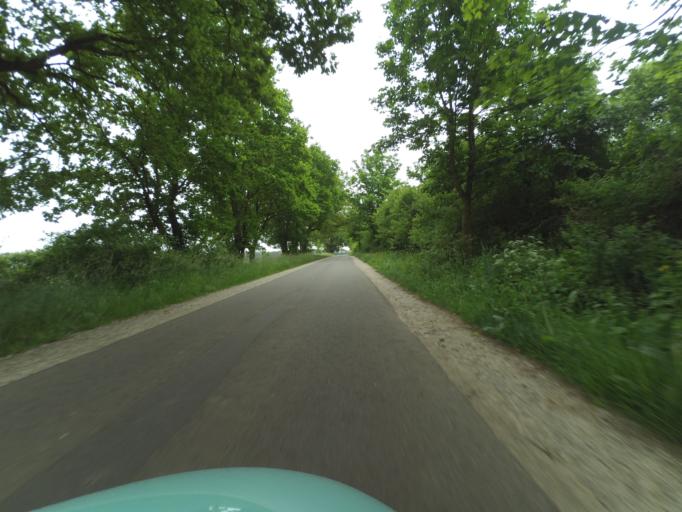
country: DE
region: Lower Saxony
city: Uetze
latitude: 52.4830
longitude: 10.1978
